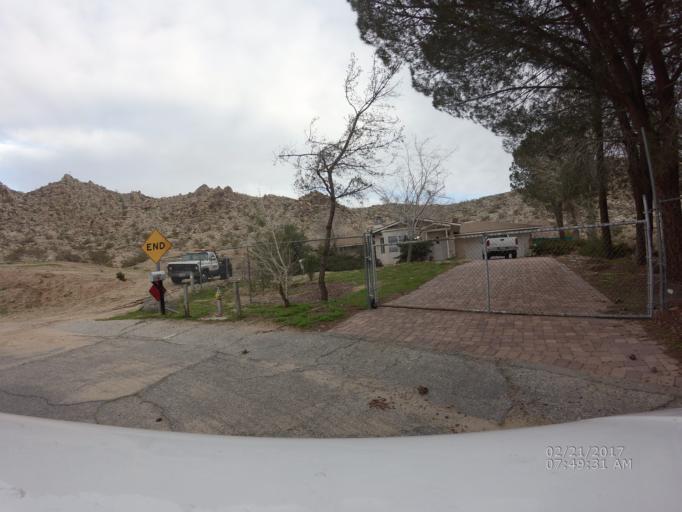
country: US
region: California
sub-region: Los Angeles County
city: Lake Los Angeles
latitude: 34.6028
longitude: -117.8428
